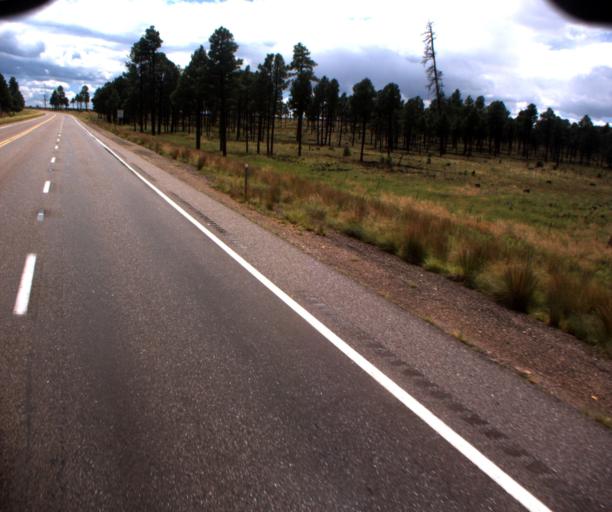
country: US
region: Arizona
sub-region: Navajo County
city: Heber-Overgaard
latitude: 34.3700
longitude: -110.4545
